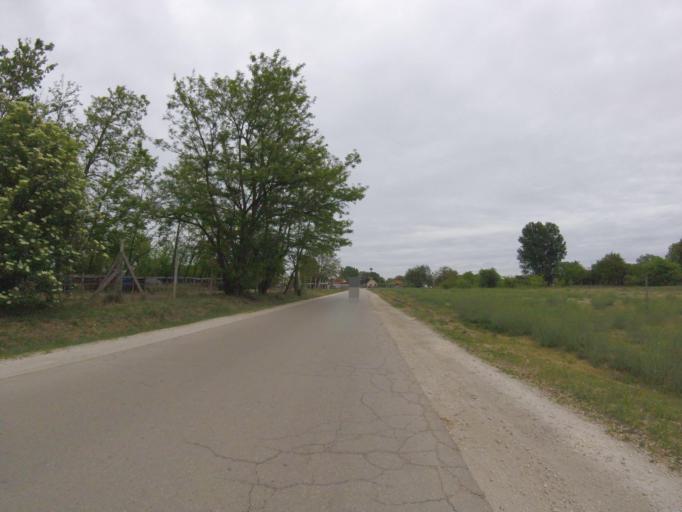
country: HU
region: Pest
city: Ujhartyan
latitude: 47.1939
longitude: 19.3774
